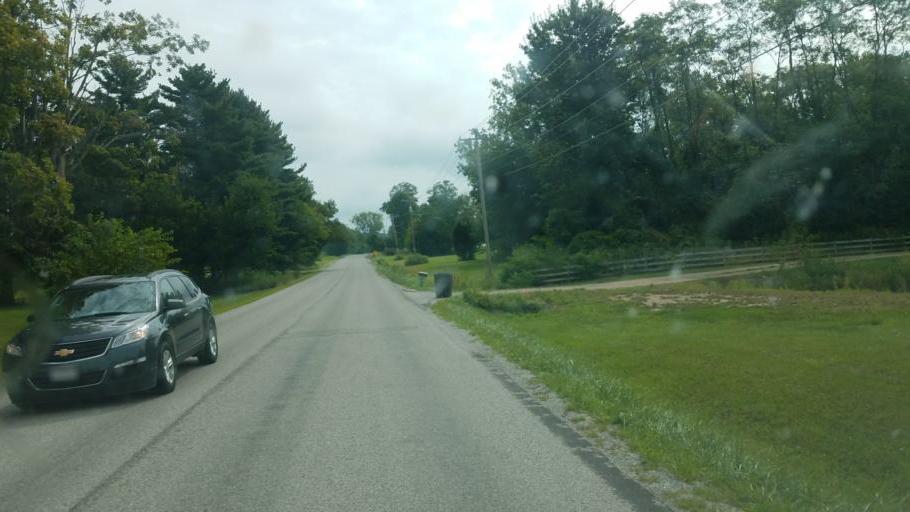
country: US
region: Ohio
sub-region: Delaware County
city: Ashley
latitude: 40.4060
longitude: -82.8586
